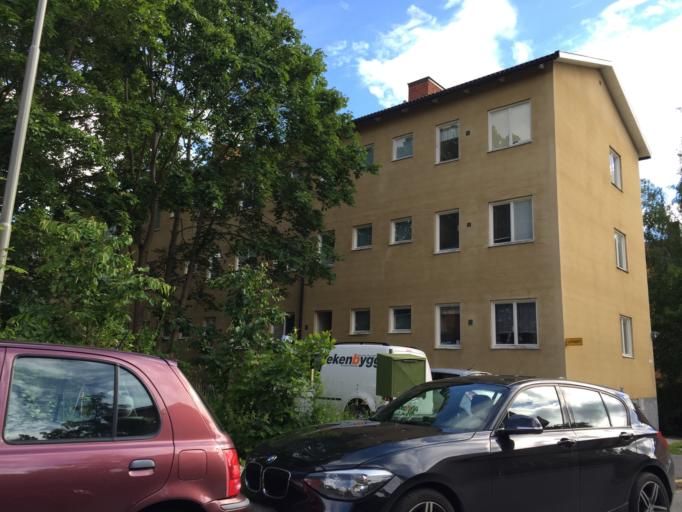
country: SE
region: Stockholm
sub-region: Stockholms Kommun
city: Arsta
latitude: 59.2945
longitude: 18.0562
